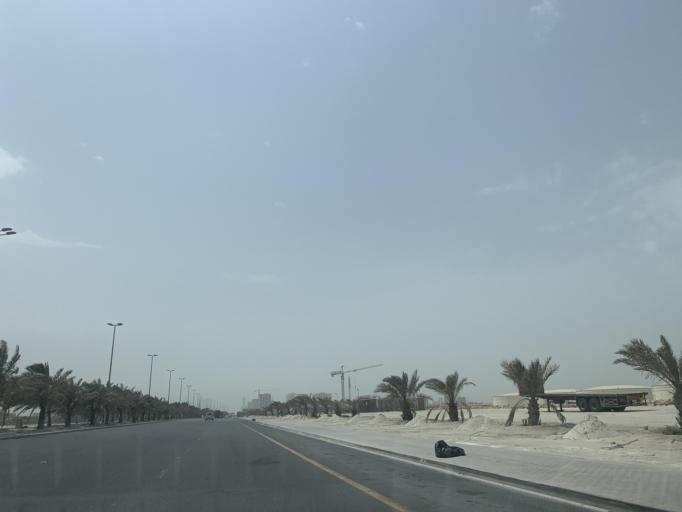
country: BH
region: Muharraq
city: Al Hadd
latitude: 26.2255
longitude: 50.6682
